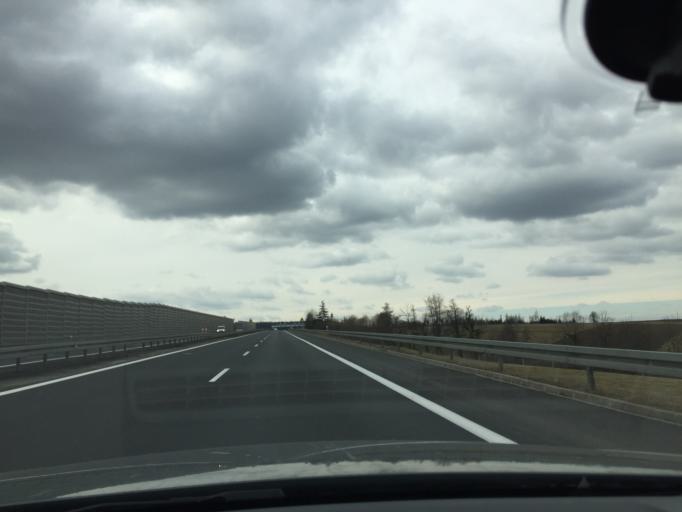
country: PL
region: Silesian Voivodeship
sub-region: Powiat cieszynski
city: Debowiec
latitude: 49.7808
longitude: 18.7400
